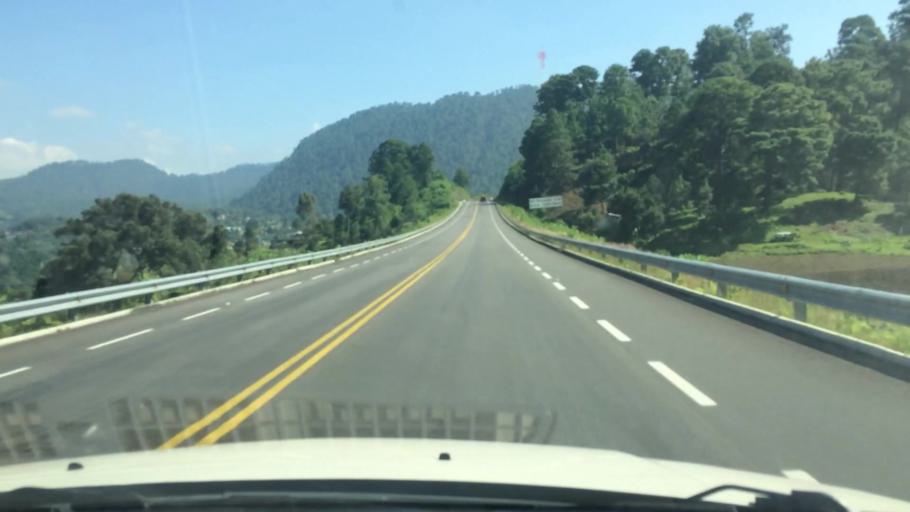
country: MX
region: Mexico
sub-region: Amanalco
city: Polvillos (San Bartolo Quinta Seccion)
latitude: 19.2241
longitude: -100.0851
